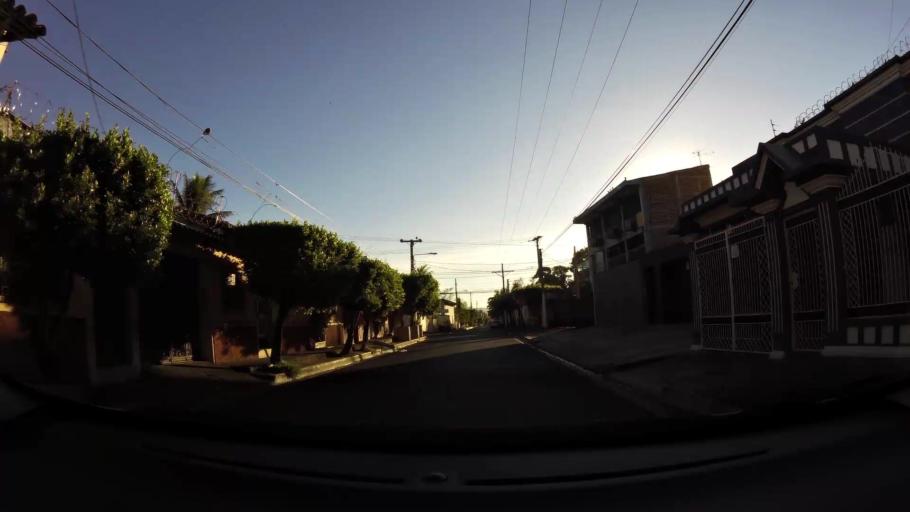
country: SV
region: San Miguel
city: San Miguel
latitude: 13.4868
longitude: -88.1837
